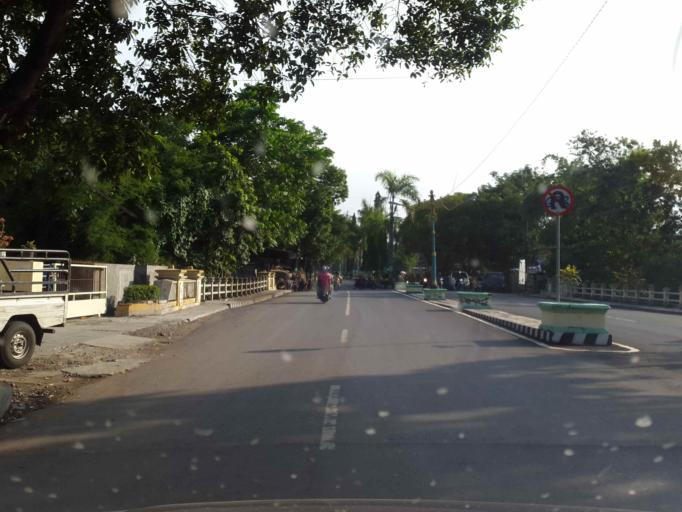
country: ID
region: Central Java
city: Slawi
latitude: -6.9802
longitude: 109.1272
